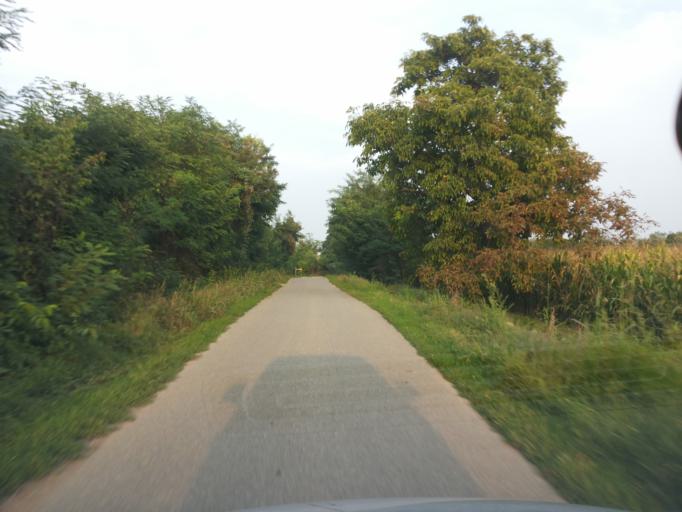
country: IT
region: Piedmont
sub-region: Provincia di Biella
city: Cavaglia
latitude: 45.3977
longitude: 8.0974
